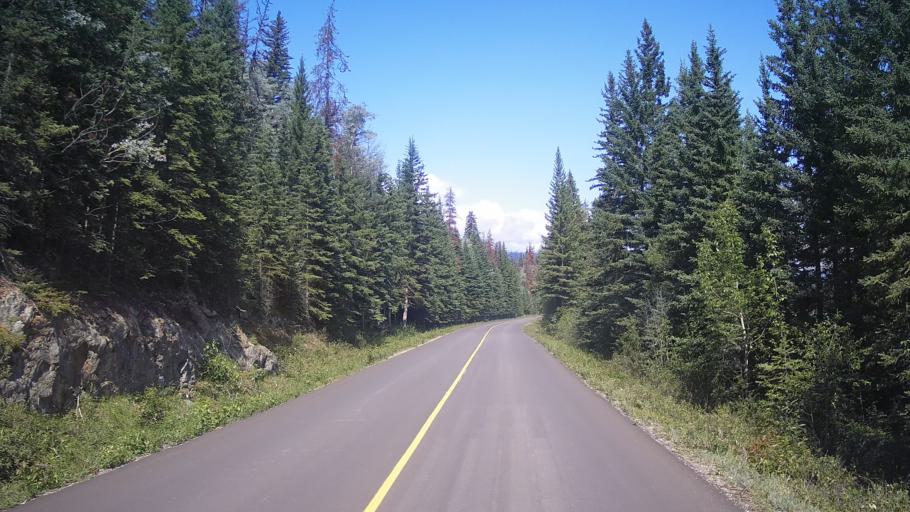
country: CA
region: Alberta
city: Jasper Park Lodge
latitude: 52.7431
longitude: -117.9679
